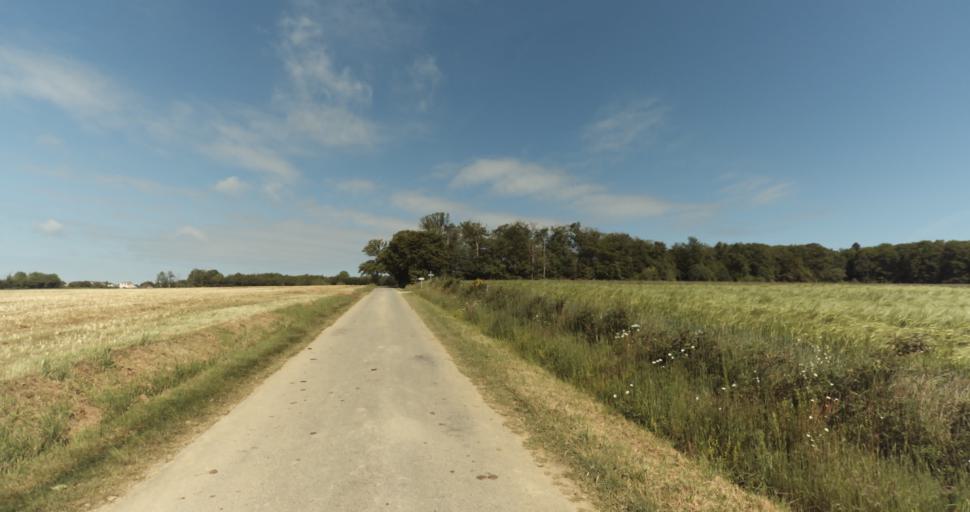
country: FR
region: Limousin
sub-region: Departement de la Haute-Vienne
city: Solignac
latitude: 45.7207
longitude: 1.2599
